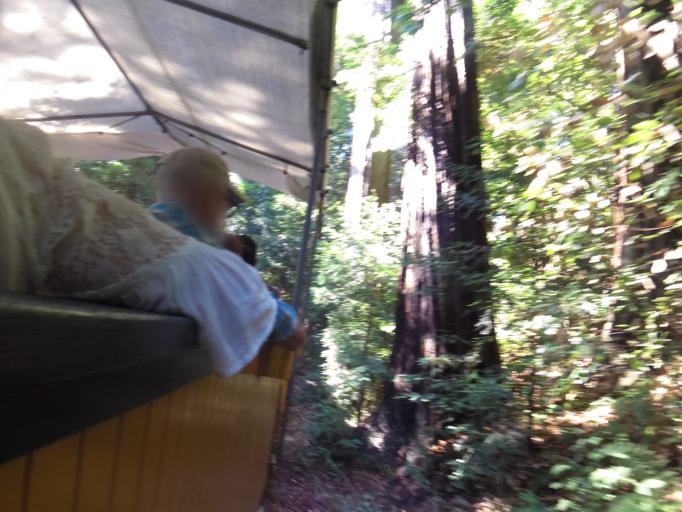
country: US
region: California
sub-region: Santa Cruz County
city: Mount Hermon
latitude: 37.0438
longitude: -122.0603
